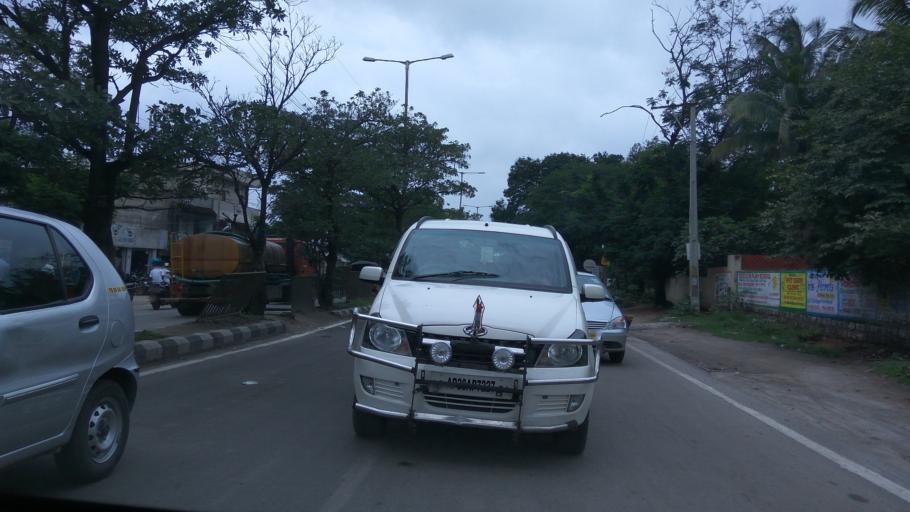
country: IN
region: Telangana
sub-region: Rangareddi
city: Secunderabad
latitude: 17.4841
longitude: 78.5487
